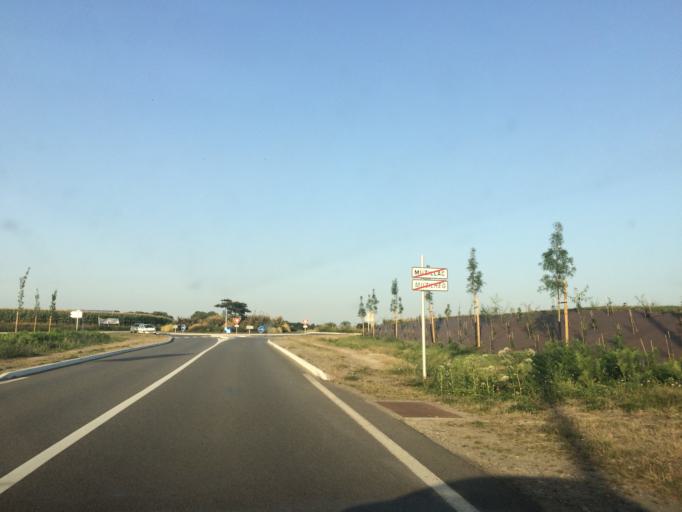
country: FR
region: Brittany
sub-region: Departement du Morbihan
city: Muzillac
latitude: 47.5606
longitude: -2.4679
